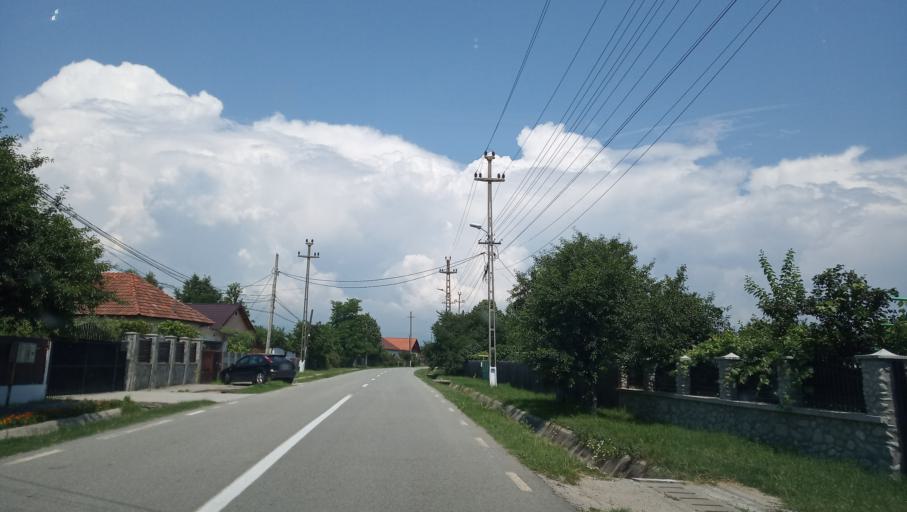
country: RO
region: Gorj
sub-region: Comuna Turcinesti
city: Turcinesti
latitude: 45.0648
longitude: 23.3479
